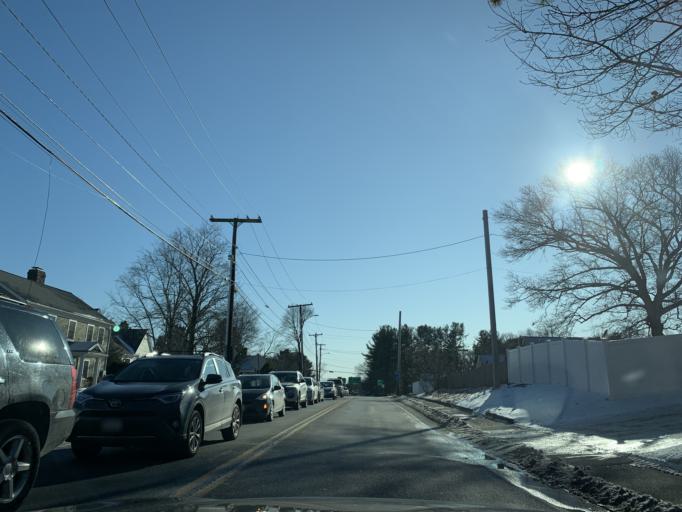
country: US
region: Massachusetts
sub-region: Norfolk County
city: Norwood
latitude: 42.1743
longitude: -71.1758
